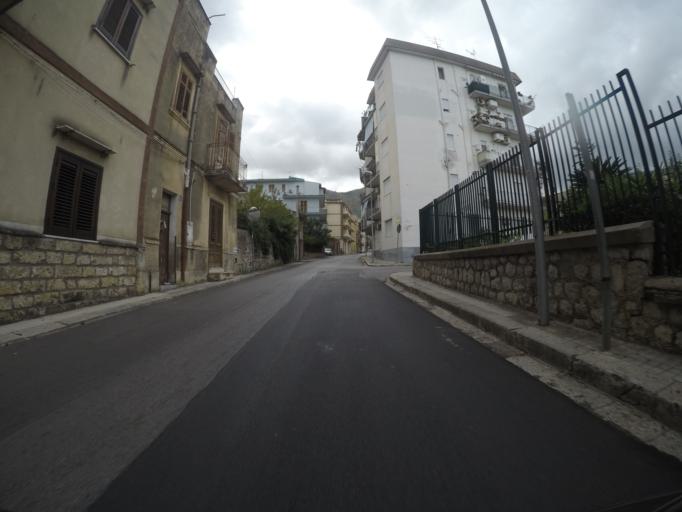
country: IT
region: Sicily
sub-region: Palermo
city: Carini
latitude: 38.1356
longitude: 13.1872
